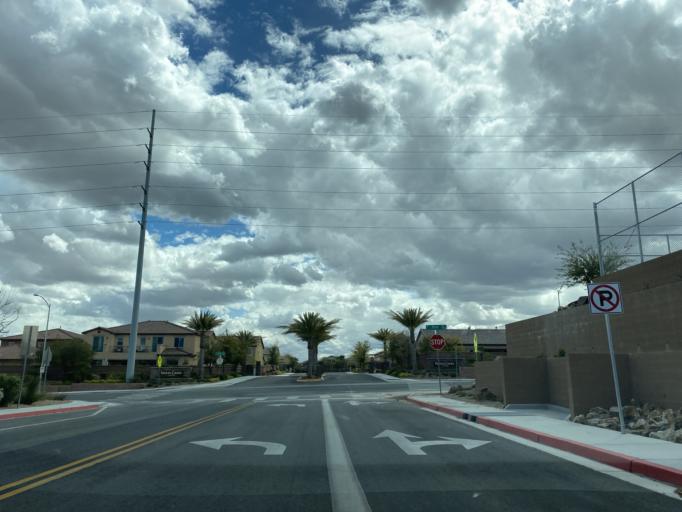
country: US
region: Nevada
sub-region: Clark County
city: Summerlin South
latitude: 36.2998
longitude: -115.3082
